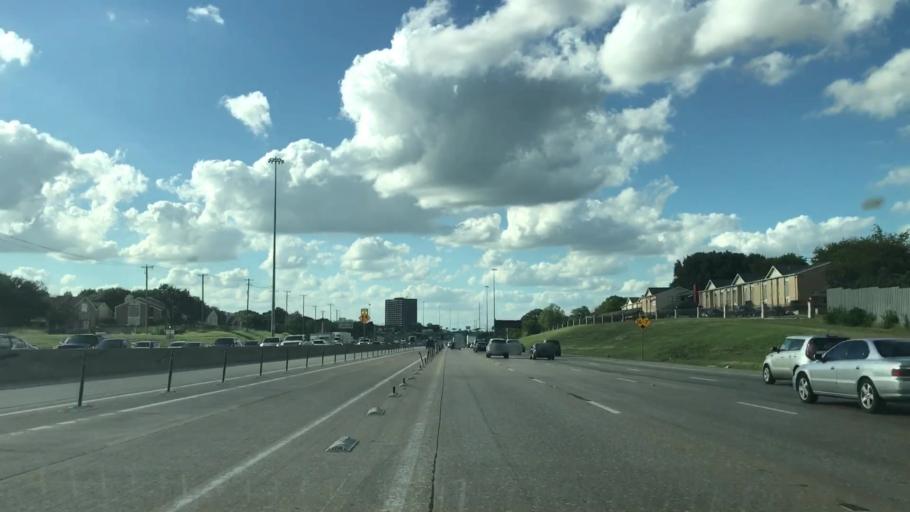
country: US
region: Texas
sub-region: Dallas County
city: Richardson
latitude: 32.9037
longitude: -96.7228
